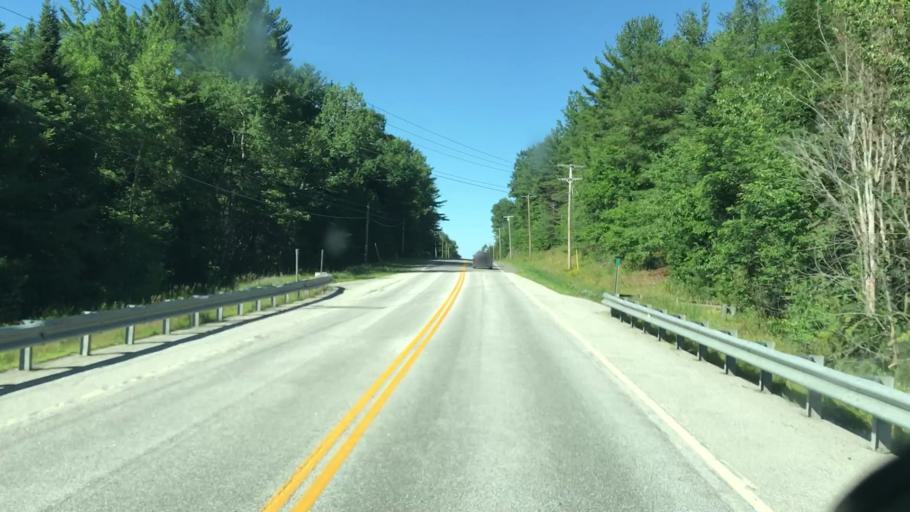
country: US
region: Maine
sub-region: Penobscot County
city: Lincoln
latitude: 45.3395
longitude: -68.5715
